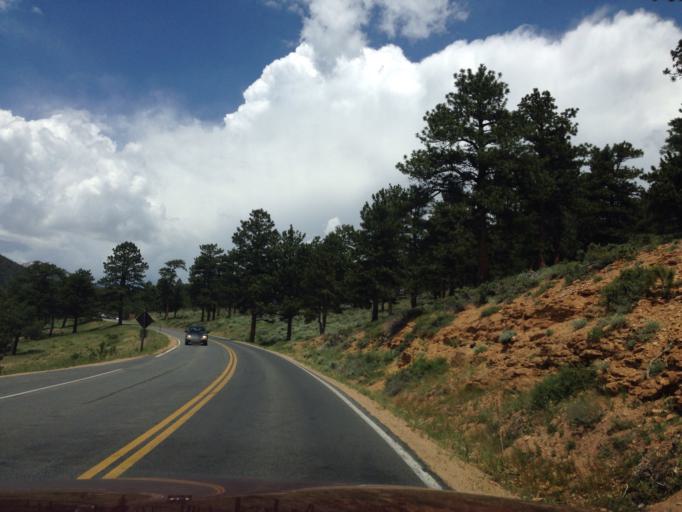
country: US
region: Colorado
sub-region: Larimer County
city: Estes Park
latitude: 40.3856
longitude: -105.6062
